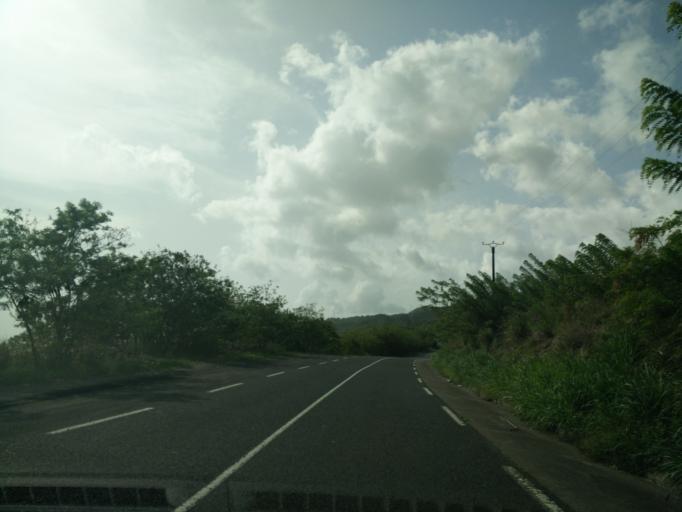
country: MQ
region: Martinique
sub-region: Martinique
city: Saint-Pierre
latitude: 14.7688
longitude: -61.1985
